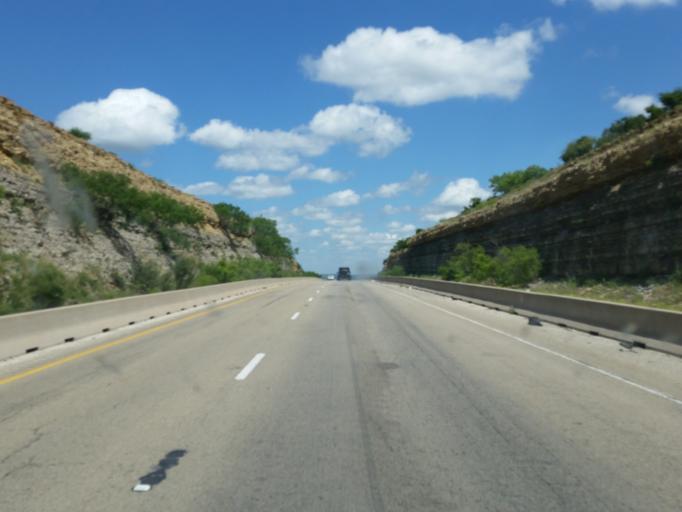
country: US
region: Texas
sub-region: Callahan County
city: Baird
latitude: 32.3954
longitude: -99.3638
